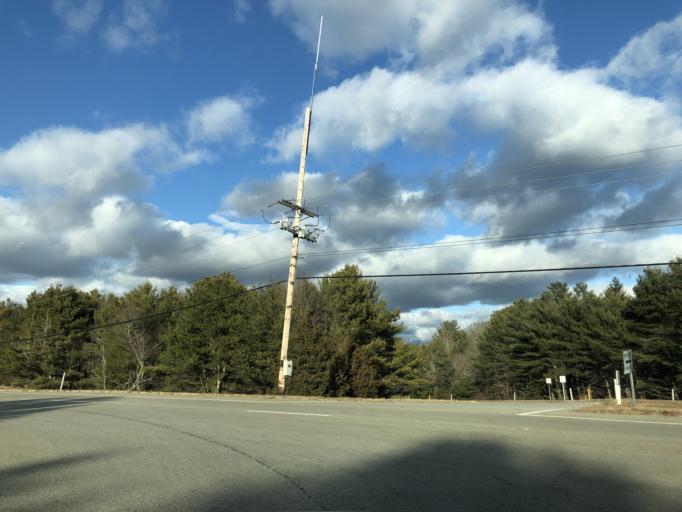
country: US
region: Massachusetts
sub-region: Plymouth County
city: Marion Center
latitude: 41.7234
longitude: -70.7752
